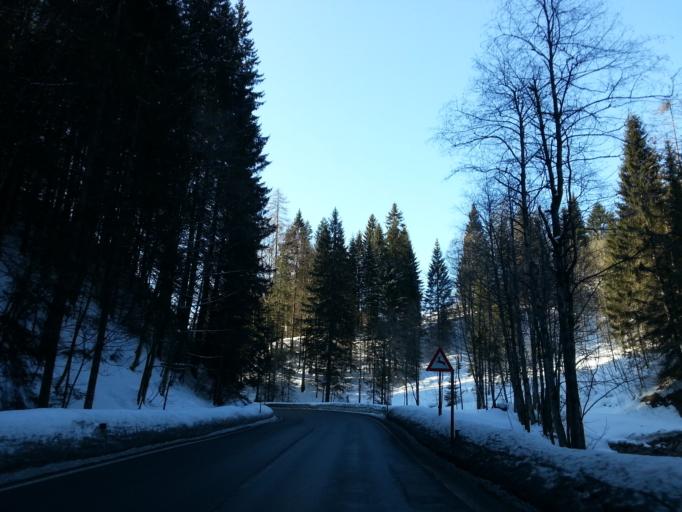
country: AT
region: Salzburg
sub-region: Politischer Bezirk Hallein
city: Abtenau
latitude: 47.4908
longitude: 13.3969
